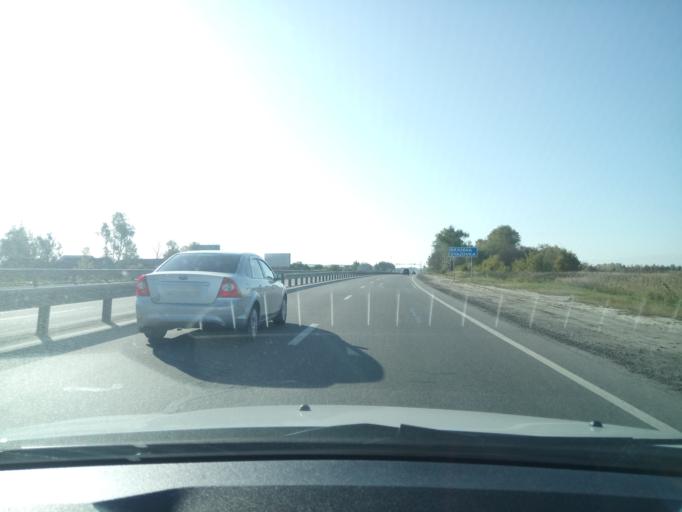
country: RU
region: Nizjnij Novgorod
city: Burevestnik
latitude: 56.1426
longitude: 43.9123
